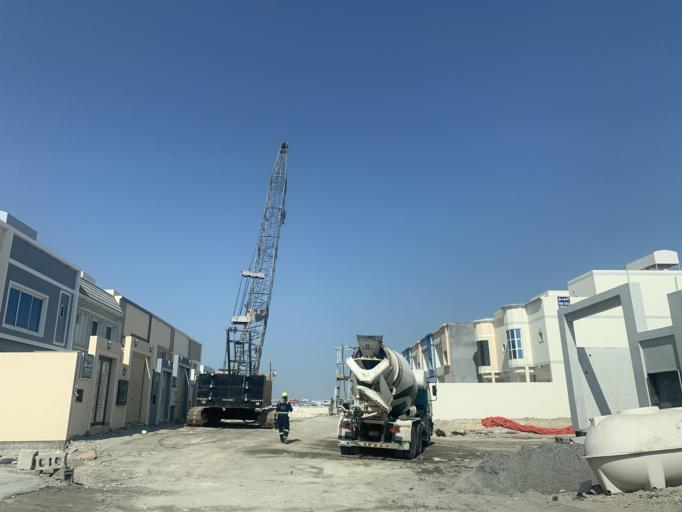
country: BH
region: Central Governorate
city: Madinat Hamad
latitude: 26.1283
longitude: 50.4861
